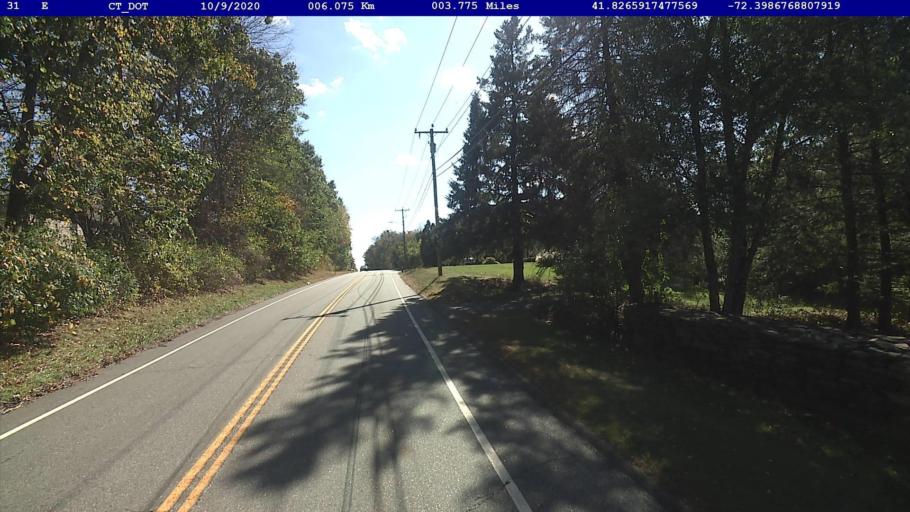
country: US
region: Connecticut
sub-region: Tolland County
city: Tolland
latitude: 41.8266
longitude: -72.3986
